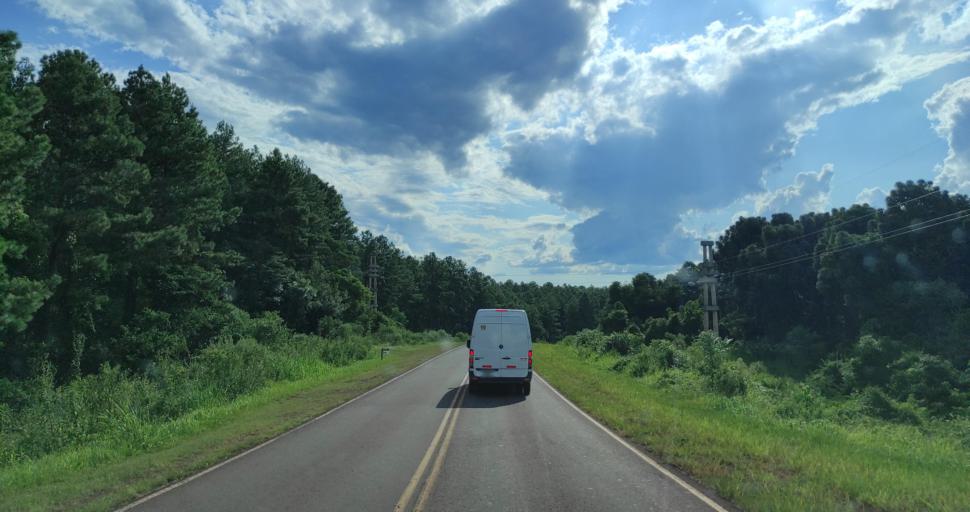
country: AR
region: Misiones
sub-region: Departamento de San Pedro
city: San Pedro
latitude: -26.3489
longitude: -53.9787
